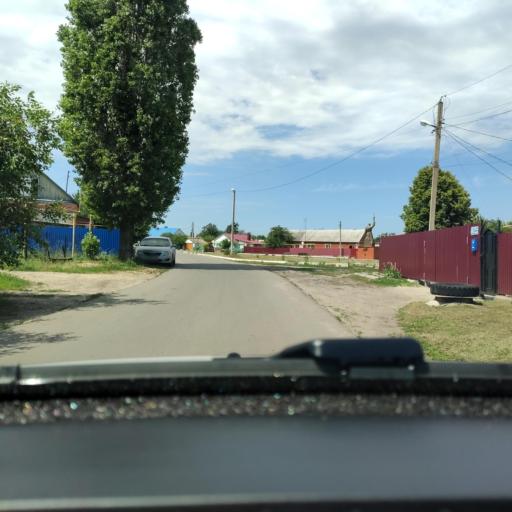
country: RU
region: Voronezj
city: Maslovka
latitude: 51.5045
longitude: 39.2975
